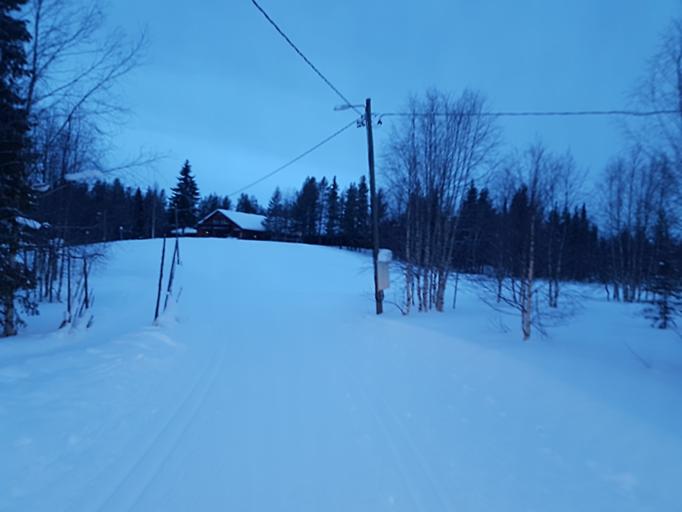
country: FI
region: Lapland
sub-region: Tunturi-Lappi
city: Kolari
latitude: 67.6162
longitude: 24.1606
